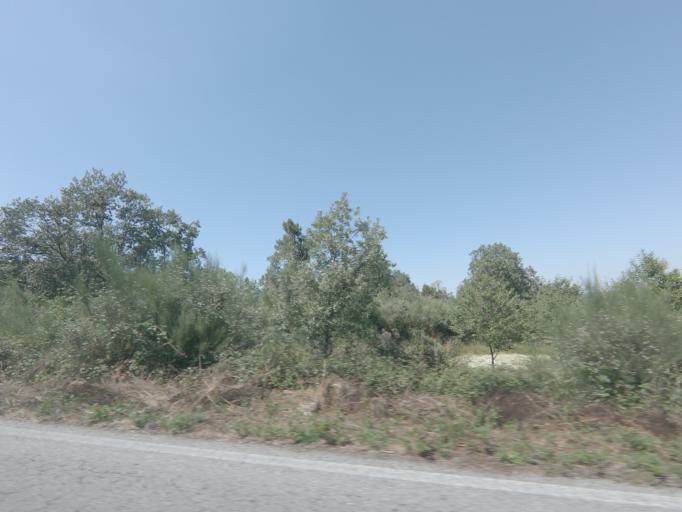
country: PT
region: Viseu
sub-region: Tarouca
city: Tarouca
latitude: 40.9915
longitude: -7.8385
